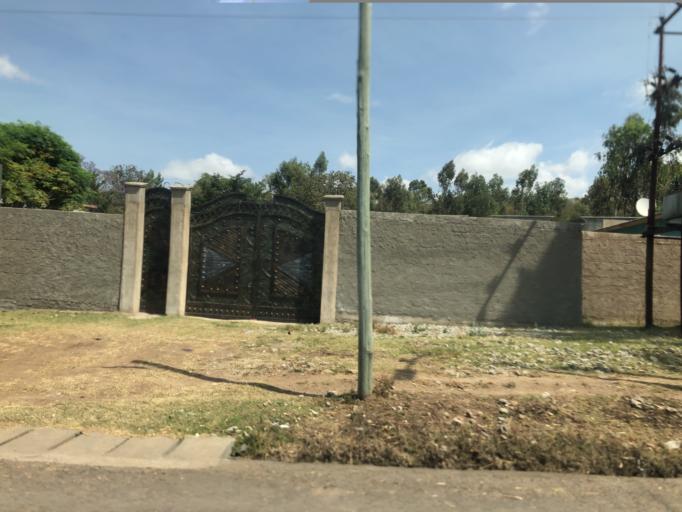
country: ET
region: Oromiya
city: Shashemene
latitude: 7.2778
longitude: 38.6536
